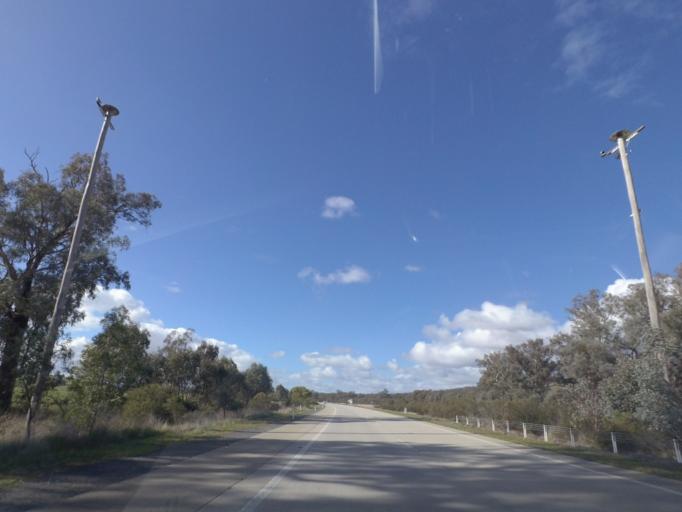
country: AU
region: New South Wales
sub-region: Albury Municipality
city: Lavington
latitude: -35.9152
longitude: 147.1460
